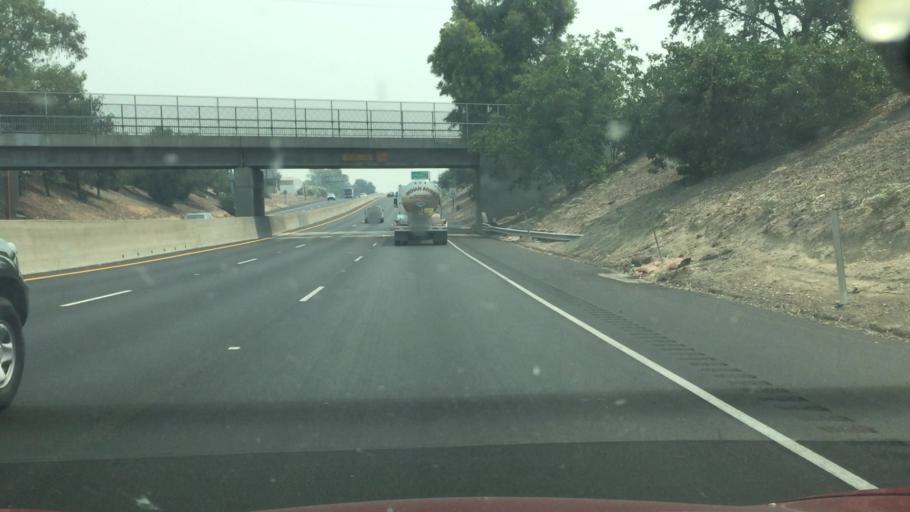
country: US
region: California
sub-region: San Joaquin County
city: August
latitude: 37.9763
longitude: -121.2486
